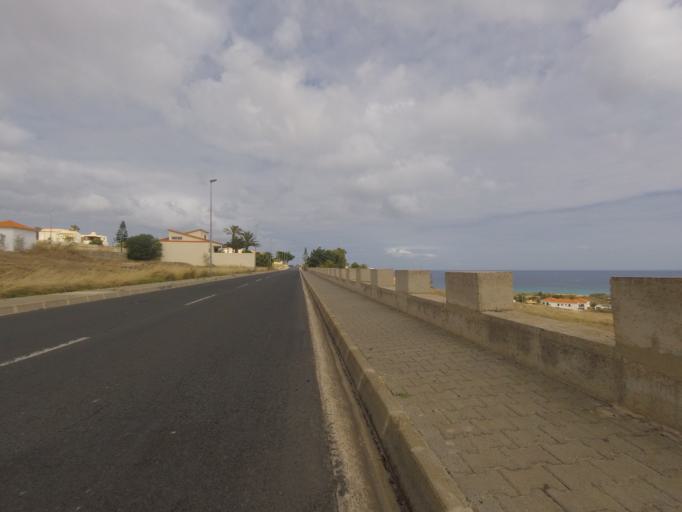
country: PT
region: Madeira
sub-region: Porto Santo
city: Vila de Porto Santo
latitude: 33.0547
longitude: -16.3479
